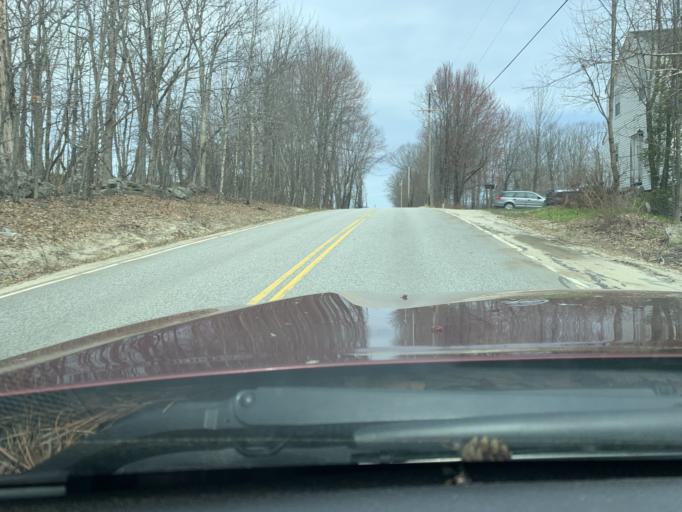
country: US
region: Maine
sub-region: Cumberland County
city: Raymond
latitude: 43.9554
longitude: -70.3872
